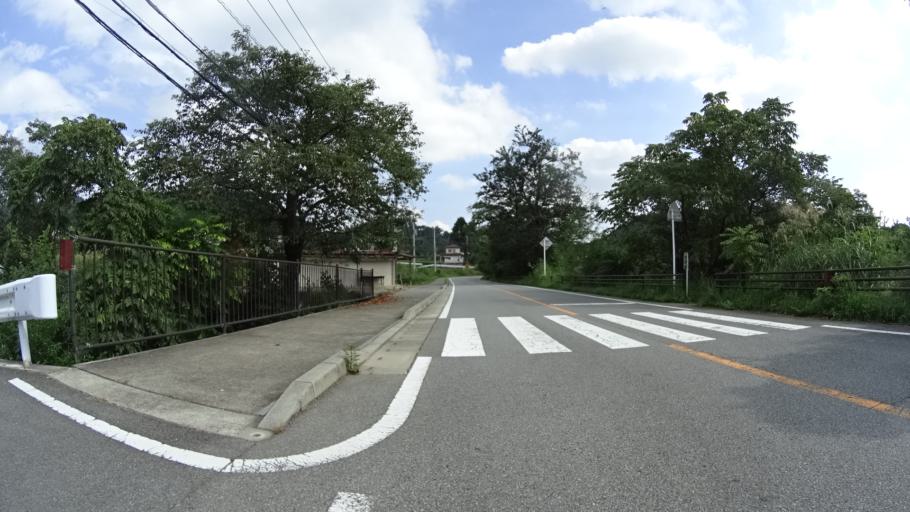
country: JP
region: Yamanashi
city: Kofu-shi
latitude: 35.7059
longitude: 138.5569
